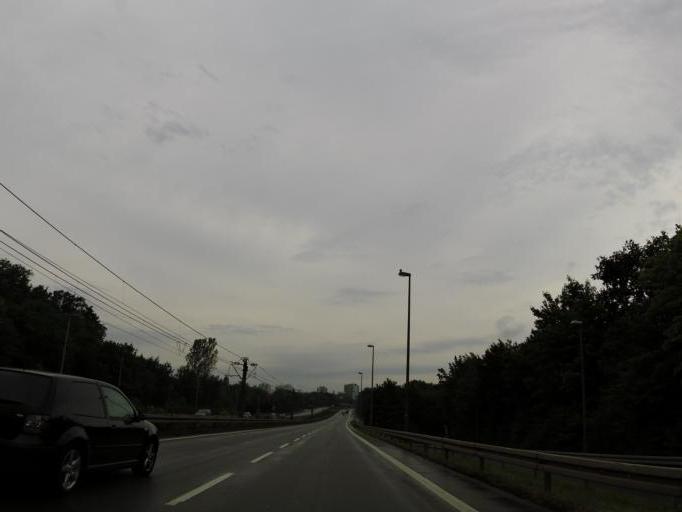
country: DE
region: Hesse
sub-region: Regierungsbezirk Darmstadt
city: Frankfurt am Main
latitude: 50.1450
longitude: 8.6414
